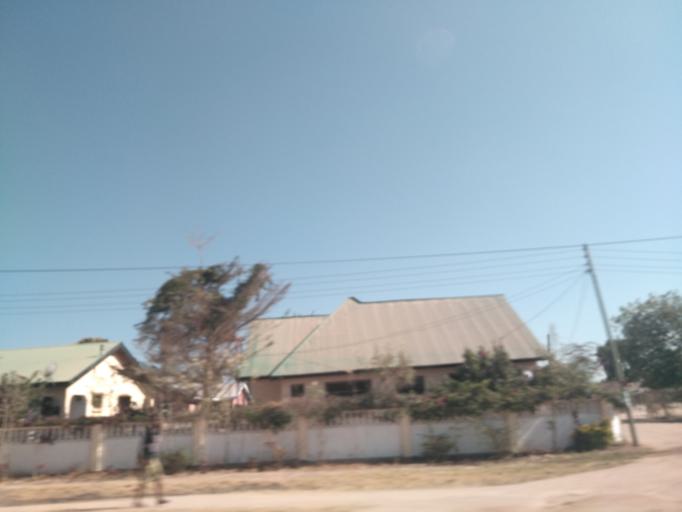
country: TZ
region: Dodoma
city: Dodoma
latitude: -6.1596
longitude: 35.7490
